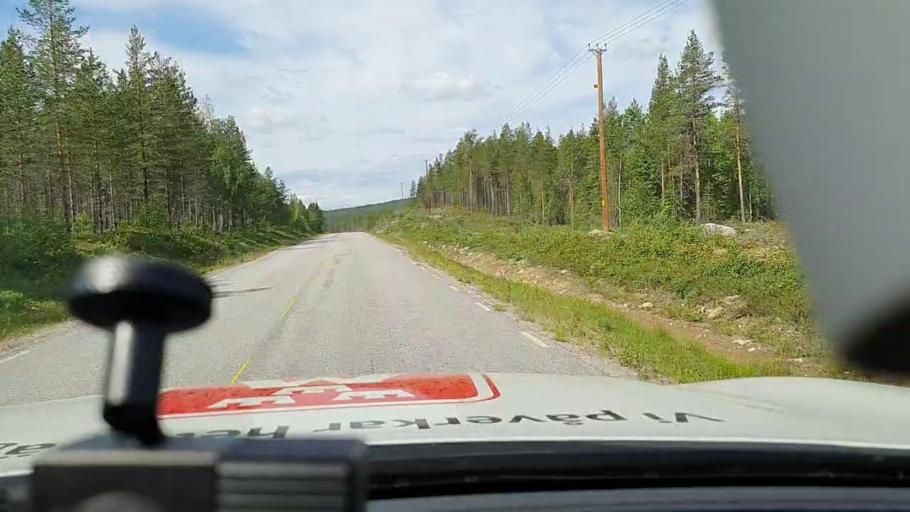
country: SE
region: Norrbotten
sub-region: Jokkmokks Kommun
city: Jokkmokk
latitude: 66.6236
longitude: 19.6744
